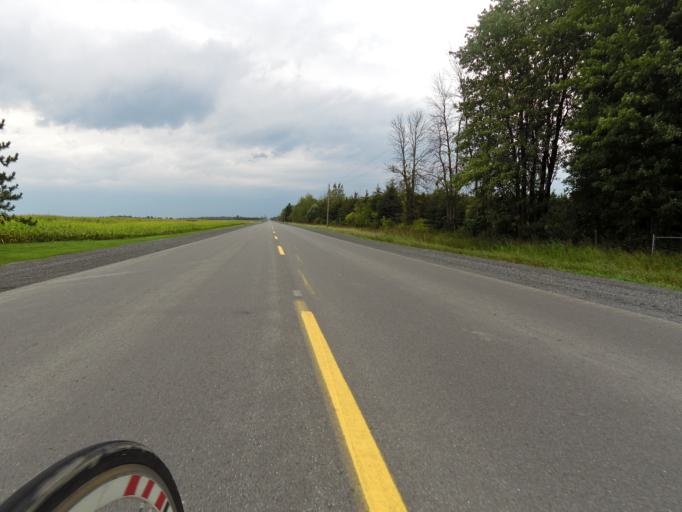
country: CA
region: Ontario
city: Bells Corners
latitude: 45.2105
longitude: -75.7687
